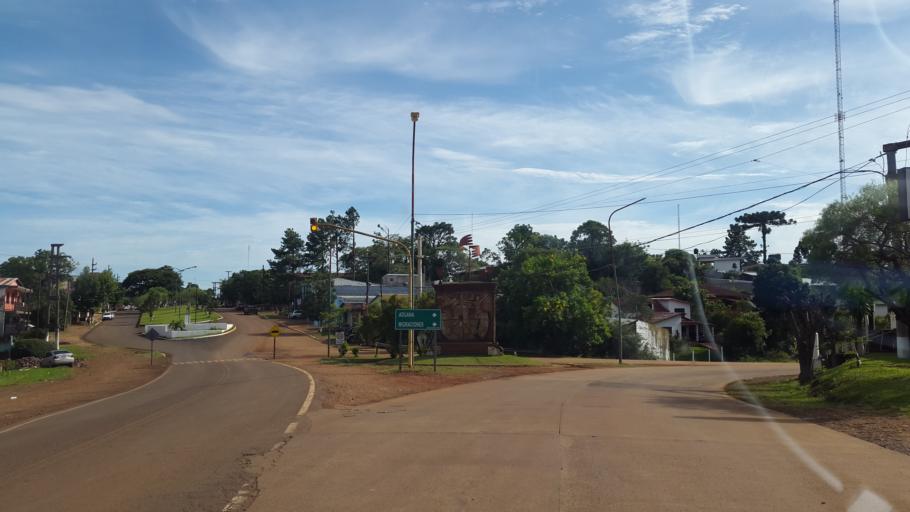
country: AR
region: Misiones
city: Bernardo de Irigoyen
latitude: -26.2604
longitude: -53.6476
